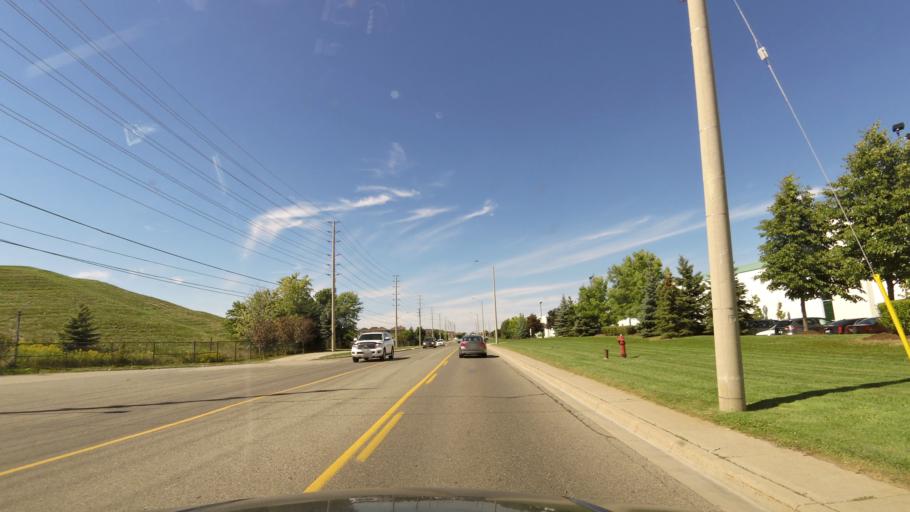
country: CA
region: Ontario
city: Mississauga
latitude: 43.6041
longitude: -79.6967
